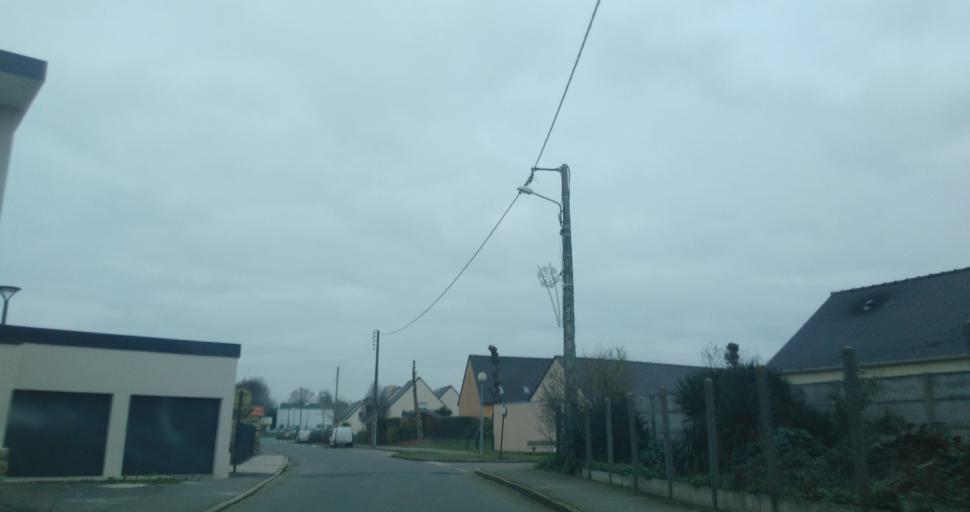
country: FR
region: Brittany
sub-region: Departement d'Ille-et-Vilaine
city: Romille
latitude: 48.2175
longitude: -1.8917
